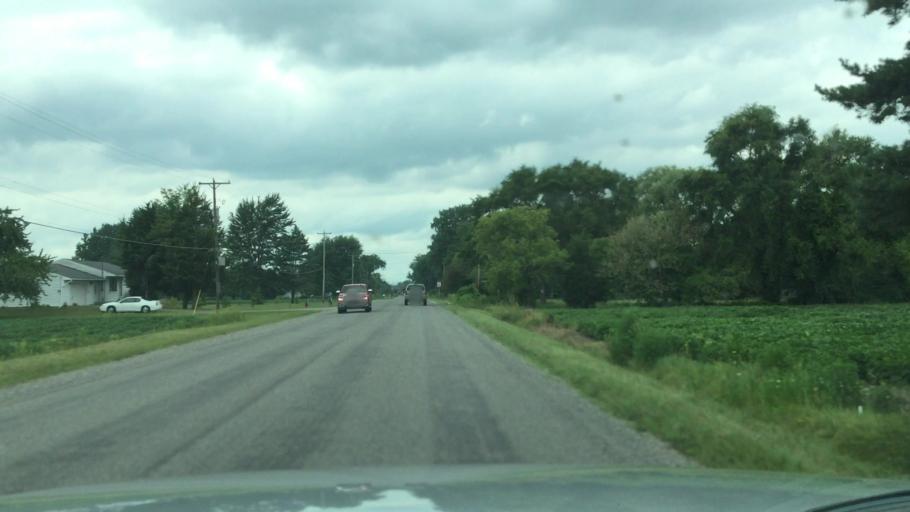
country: US
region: Michigan
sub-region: Saginaw County
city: Birch Run
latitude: 43.2504
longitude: -83.8213
